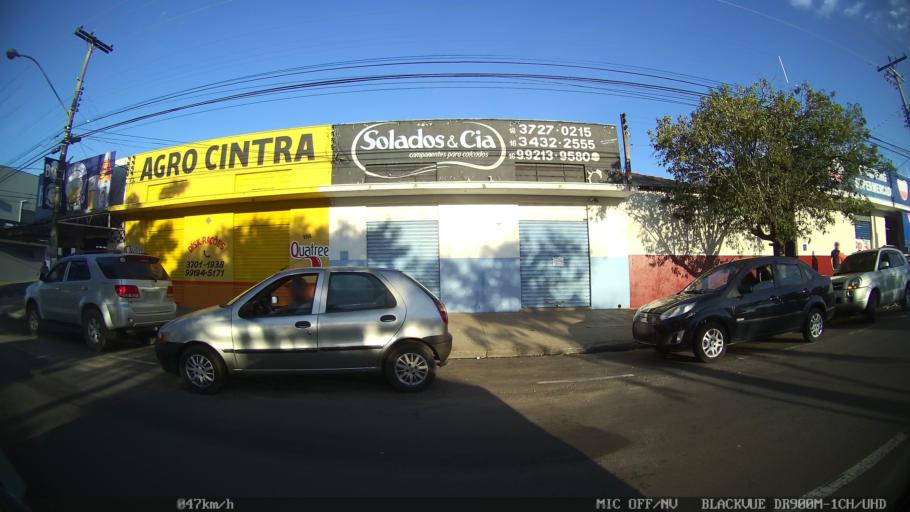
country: BR
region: Sao Paulo
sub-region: Franca
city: Franca
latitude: -20.5228
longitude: -47.3866
